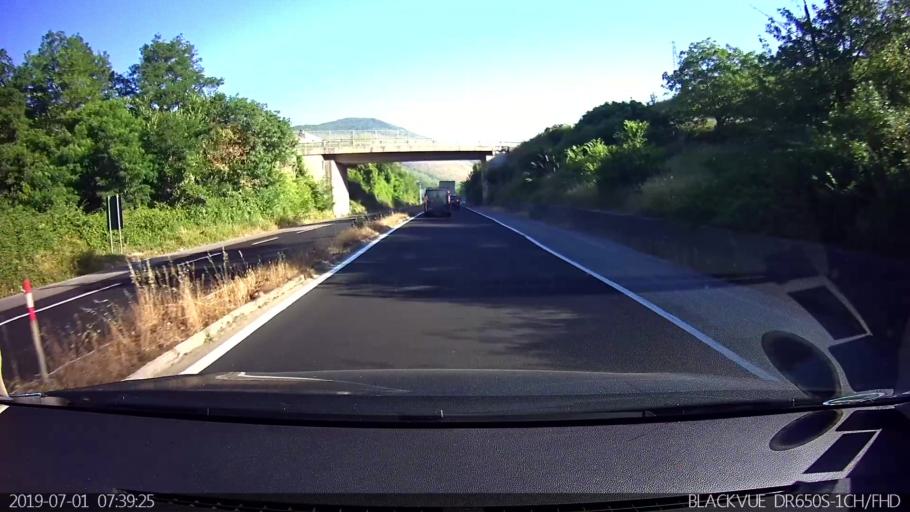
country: IT
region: Latium
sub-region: Provincia di Frosinone
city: Giuliano di Roma
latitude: 41.5493
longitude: 13.2687
